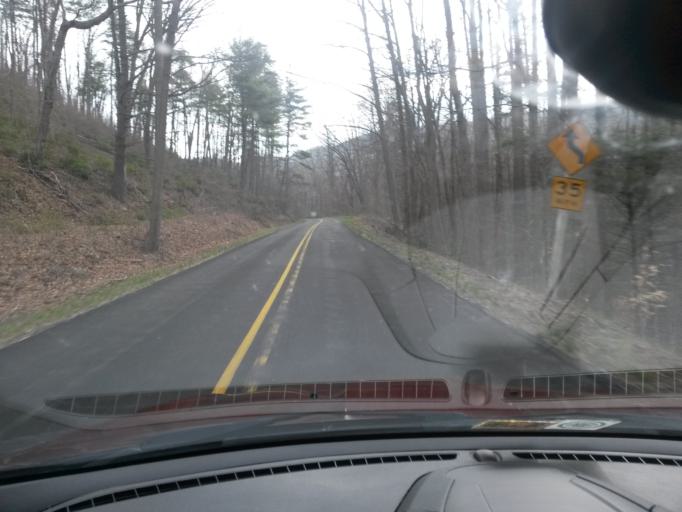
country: US
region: Virginia
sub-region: Alleghany County
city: Clifton Forge
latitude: 37.8378
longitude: -79.6493
